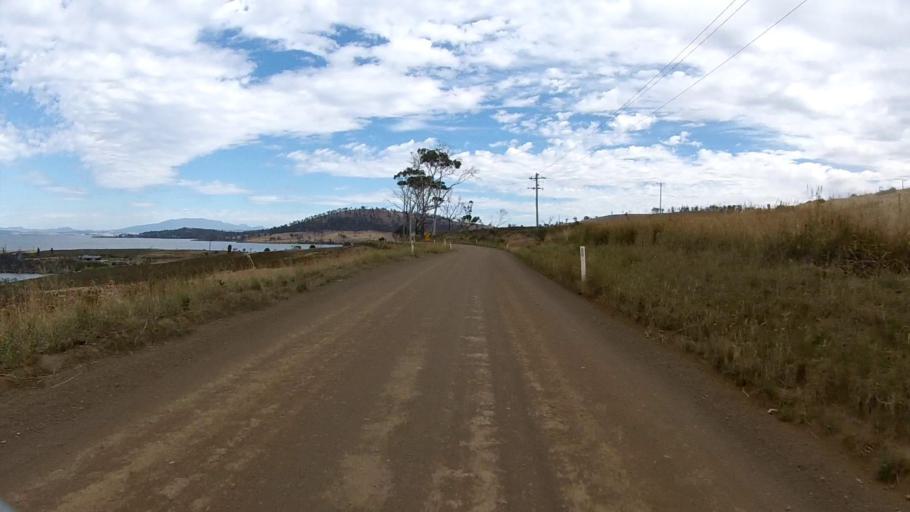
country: AU
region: Tasmania
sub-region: Sorell
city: Sorell
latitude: -42.8939
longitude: 147.7428
